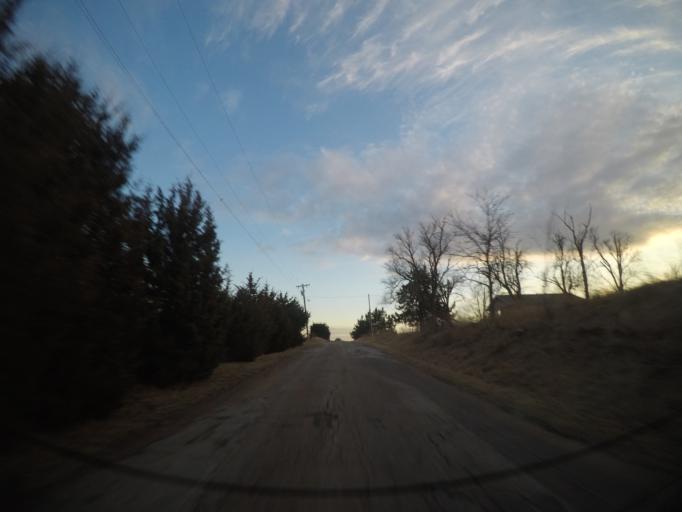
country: US
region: Kansas
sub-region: Wyandotte County
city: Bonner Springs
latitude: 39.0275
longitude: -94.9088
